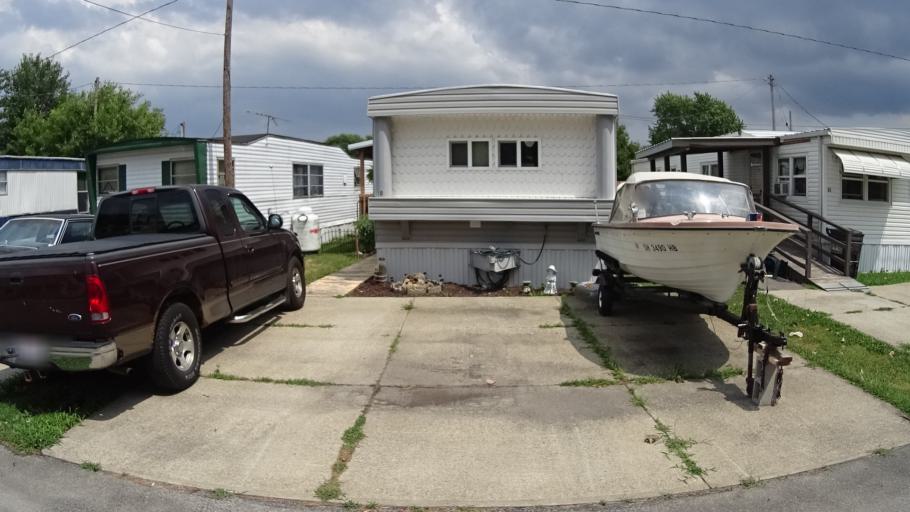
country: US
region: Ohio
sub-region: Erie County
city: Sandusky
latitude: 41.4412
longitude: -82.7554
